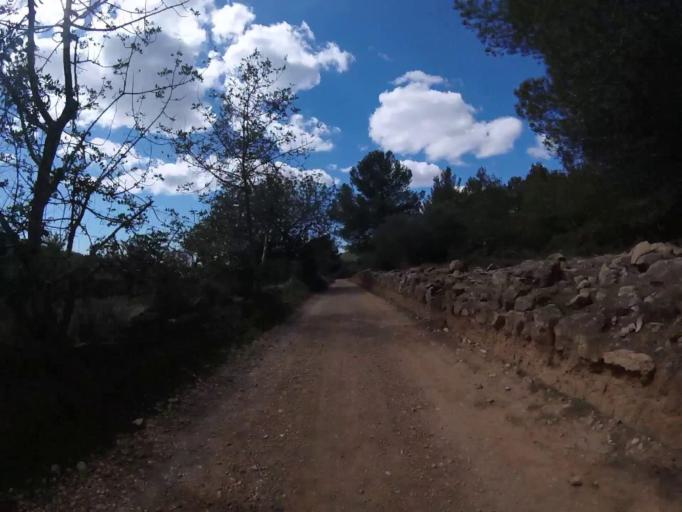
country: ES
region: Valencia
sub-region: Provincia de Castello
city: Santa Magdalena de Pulpis
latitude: 40.3219
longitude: 0.3332
